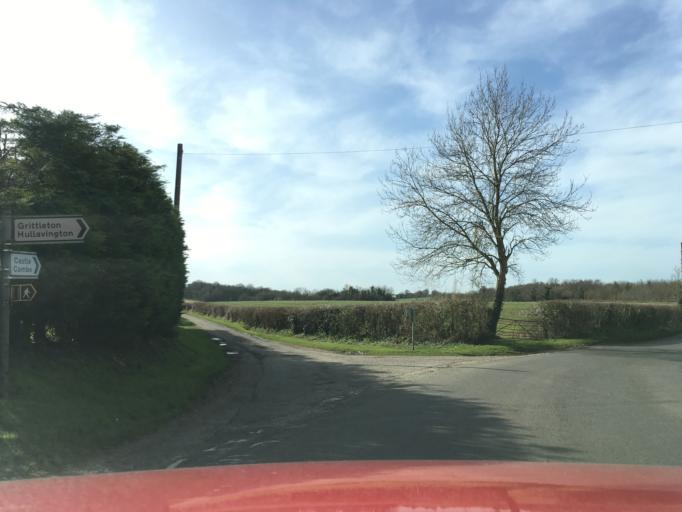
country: GB
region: England
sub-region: Wiltshire
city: Norton
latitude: 51.5206
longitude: -2.1568
